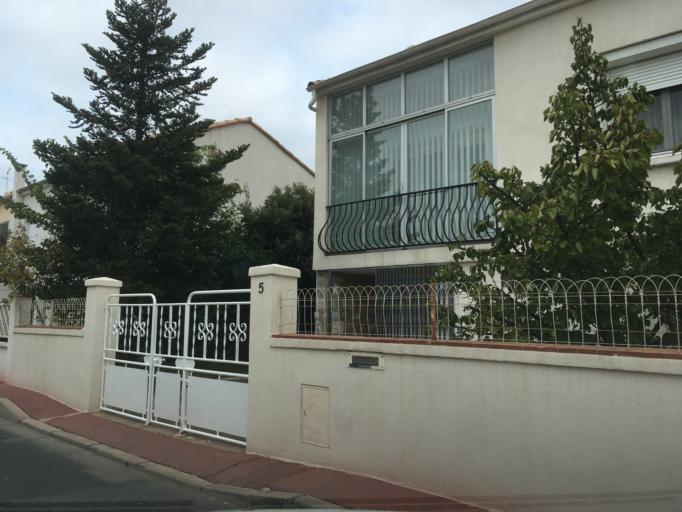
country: FR
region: Languedoc-Roussillon
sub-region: Departement de l'Herault
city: Montpellier
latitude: 43.5925
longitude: 3.8819
